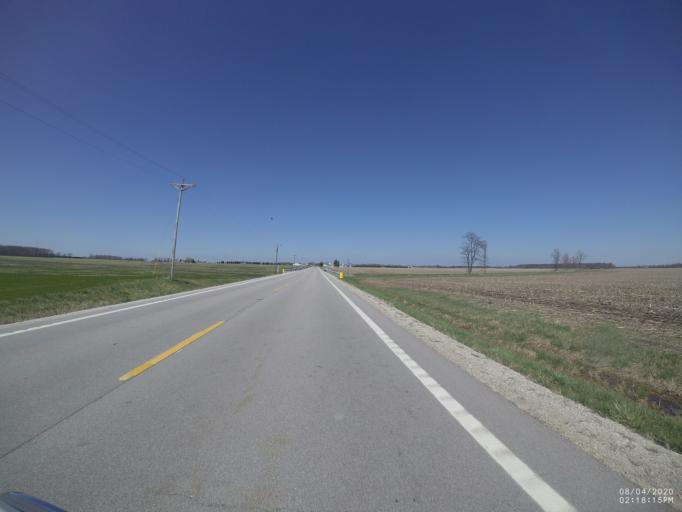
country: US
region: Ohio
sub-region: Sandusky County
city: Stony Prairie
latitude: 41.2831
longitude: -83.2353
